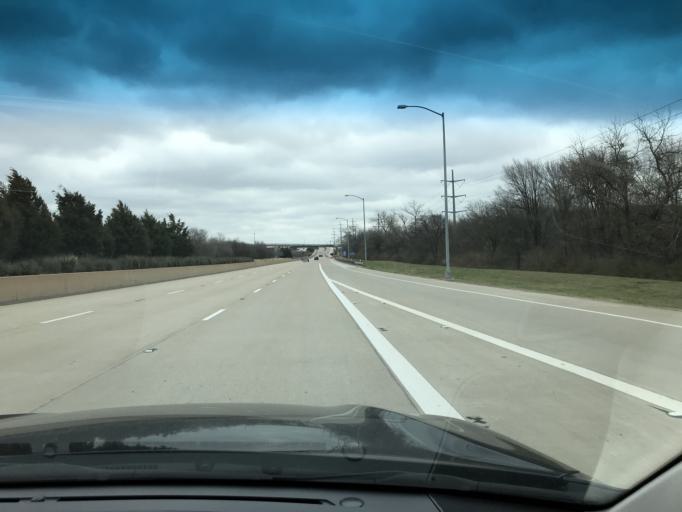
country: US
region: Texas
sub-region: Tarrant County
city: Westworth
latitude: 32.7139
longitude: -97.3951
